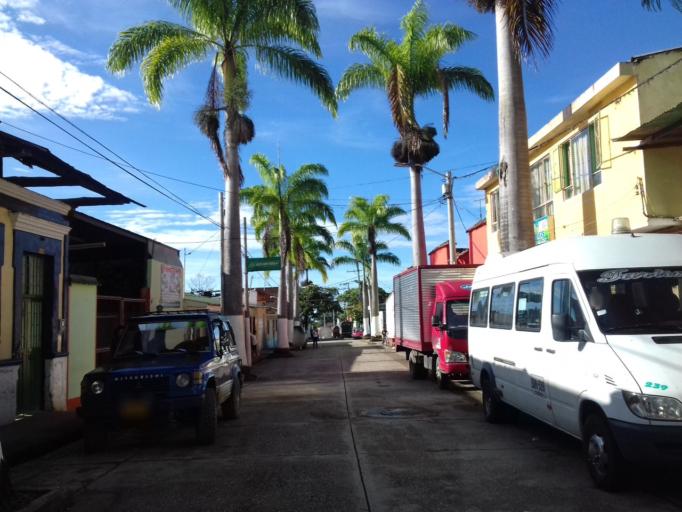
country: CO
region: Cundinamarca
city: Quipile
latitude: 4.7469
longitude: -74.5334
